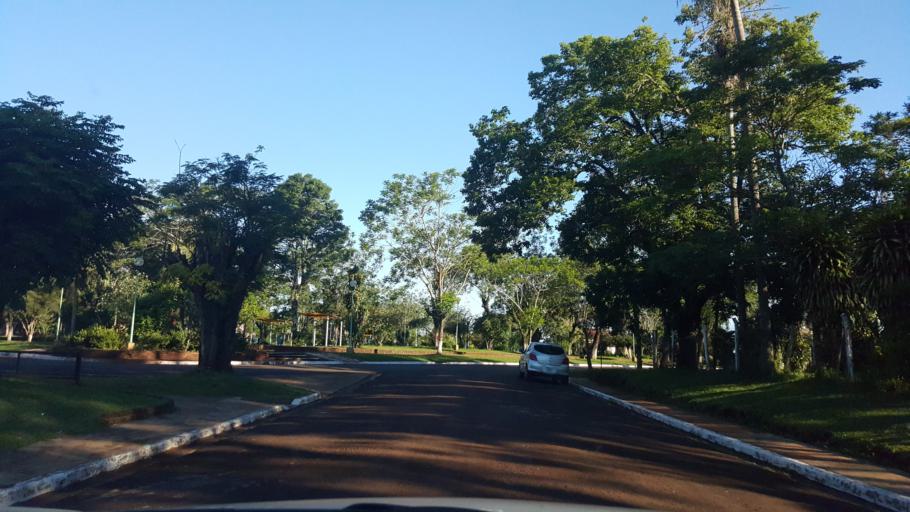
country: AR
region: Misiones
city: Gobernador Roca
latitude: -27.1289
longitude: -55.5117
